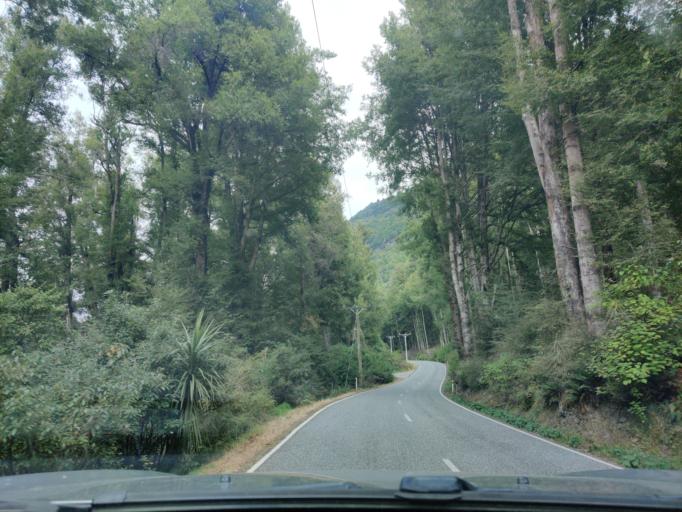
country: NZ
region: Otago
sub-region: Queenstown-Lakes District
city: Queenstown
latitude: -45.0703
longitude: 168.5026
